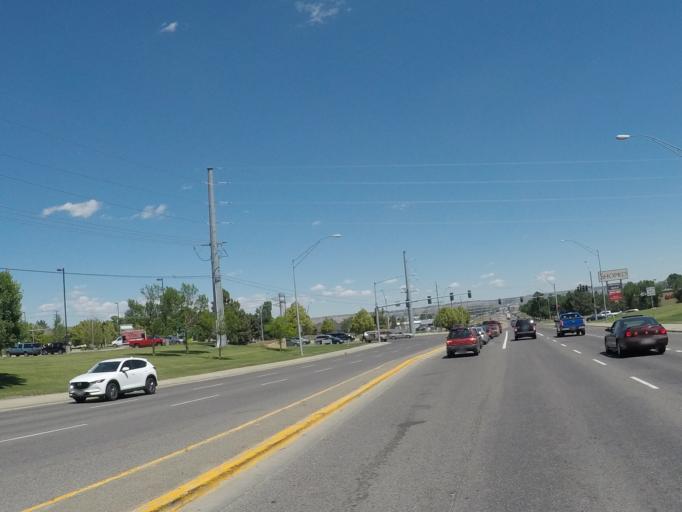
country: US
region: Montana
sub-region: Yellowstone County
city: Billings
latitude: 45.7551
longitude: -108.5778
